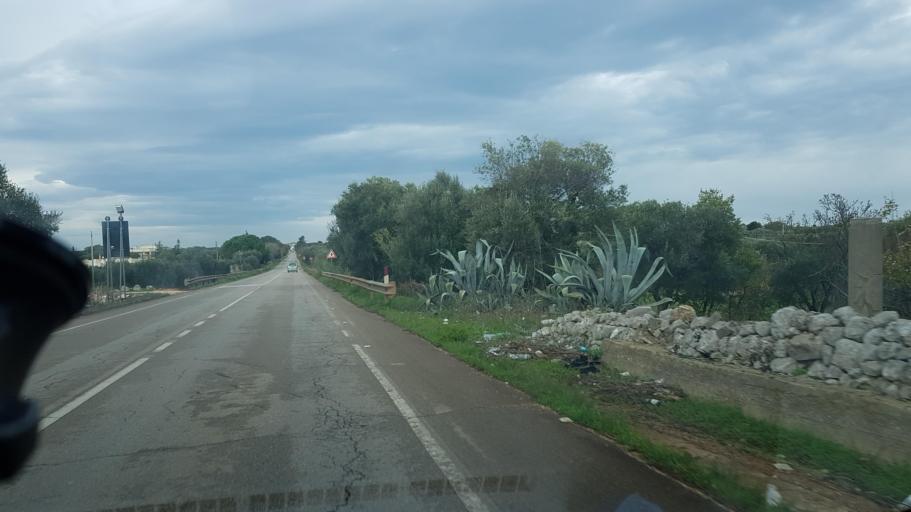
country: IT
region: Apulia
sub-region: Provincia di Brindisi
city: San Vito dei Normanni
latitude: 40.6797
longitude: 17.6848
